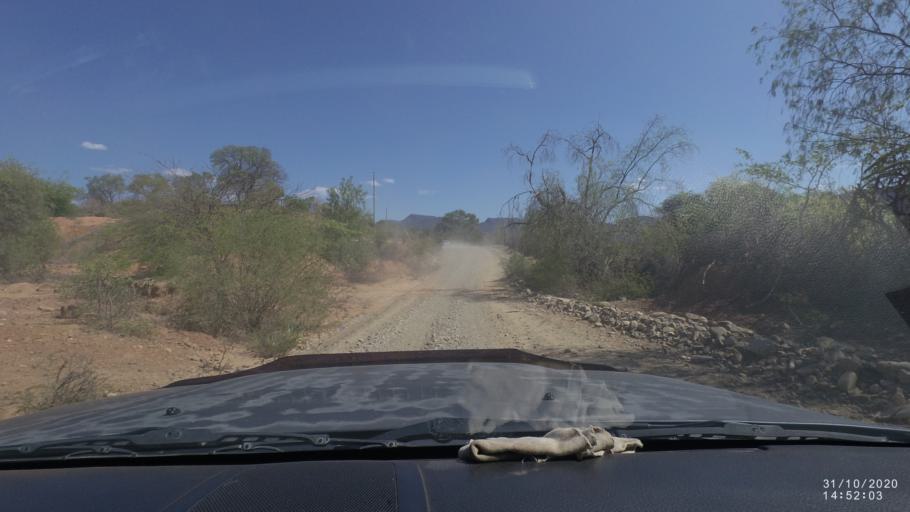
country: BO
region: Cochabamba
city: Aiquile
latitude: -18.2109
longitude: -64.8568
